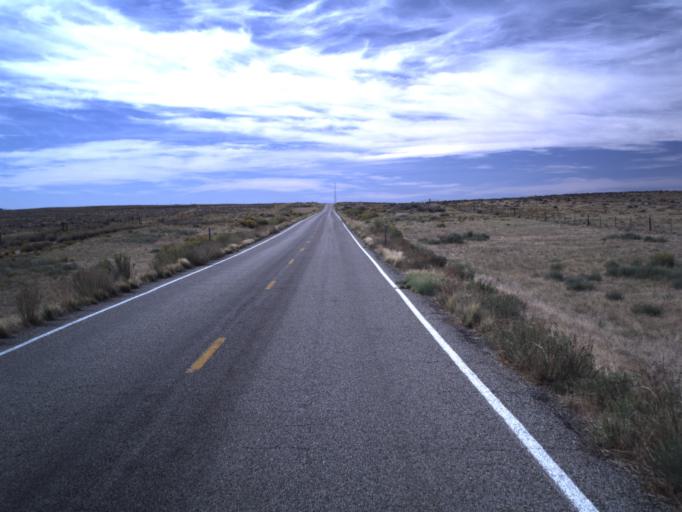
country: US
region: Utah
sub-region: San Juan County
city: Blanding
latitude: 37.3487
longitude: -109.3477
